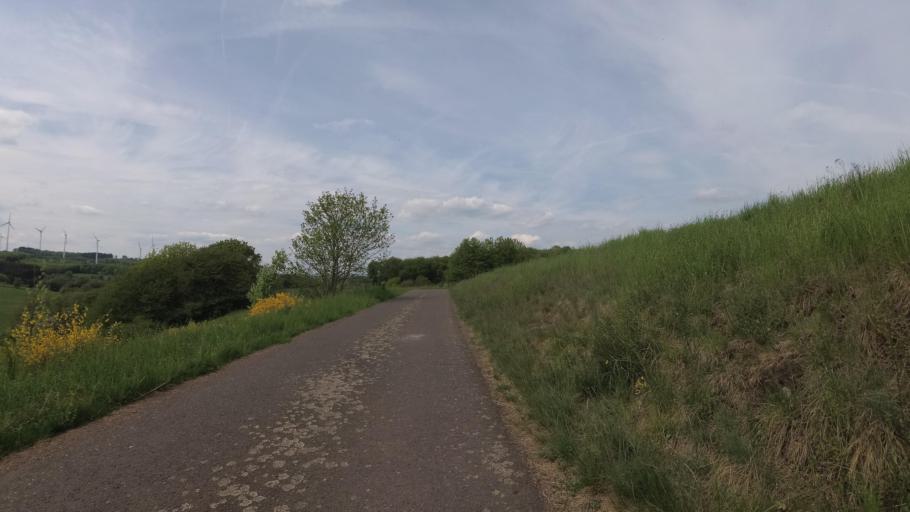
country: DE
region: Rheinland-Pfalz
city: Eckersweiler
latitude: 49.5626
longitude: 7.2959
